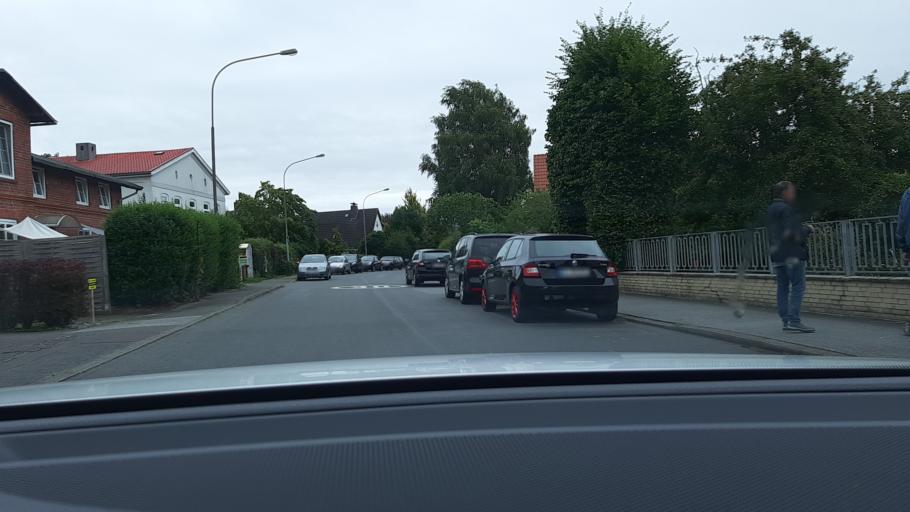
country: DE
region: Schleswig-Holstein
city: Bad Schwartau
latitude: 53.9011
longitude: 10.7398
